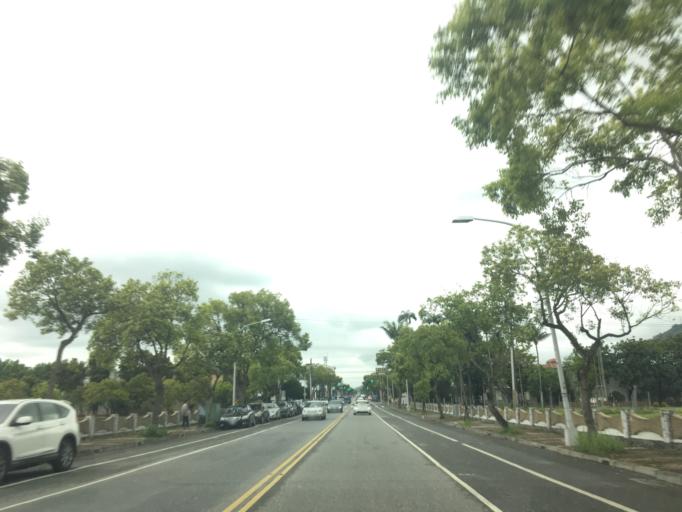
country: TW
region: Taiwan
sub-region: Hualien
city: Hualian
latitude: 23.9759
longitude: 121.5648
